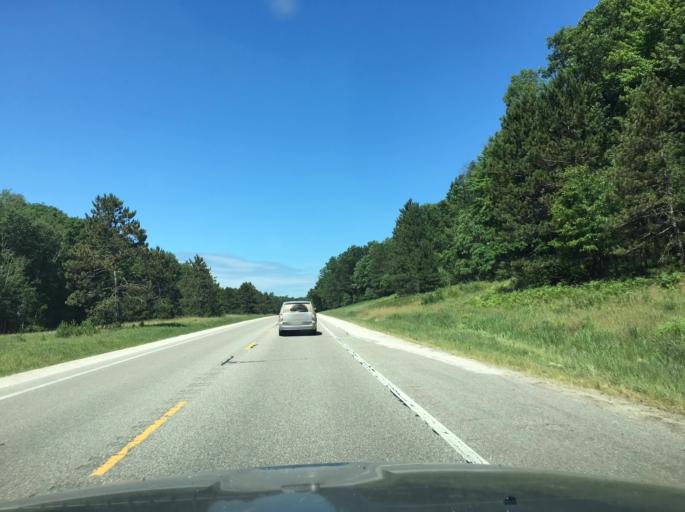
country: US
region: Michigan
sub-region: Osceola County
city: Reed City
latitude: 43.8923
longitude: -85.6719
